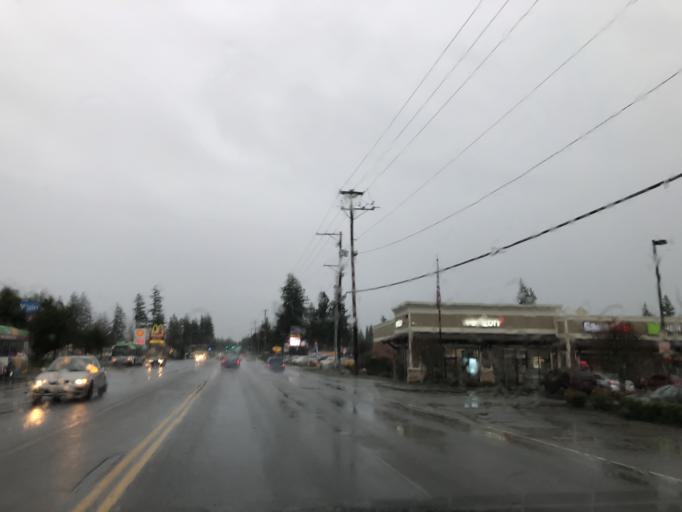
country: US
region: Washington
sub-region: Pierce County
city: Elk Plain
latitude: 47.0733
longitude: -122.4212
